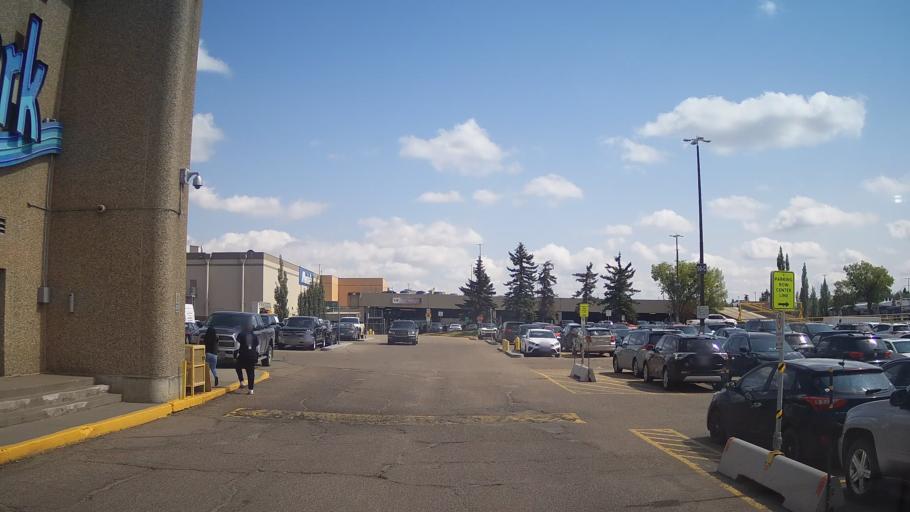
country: CA
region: Alberta
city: St. Albert
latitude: 53.5214
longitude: -113.6249
